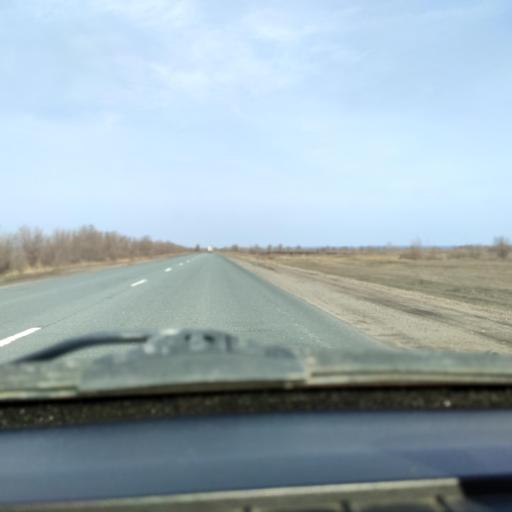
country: RU
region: Samara
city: Kinel'
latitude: 53.1626
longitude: 50.5140
